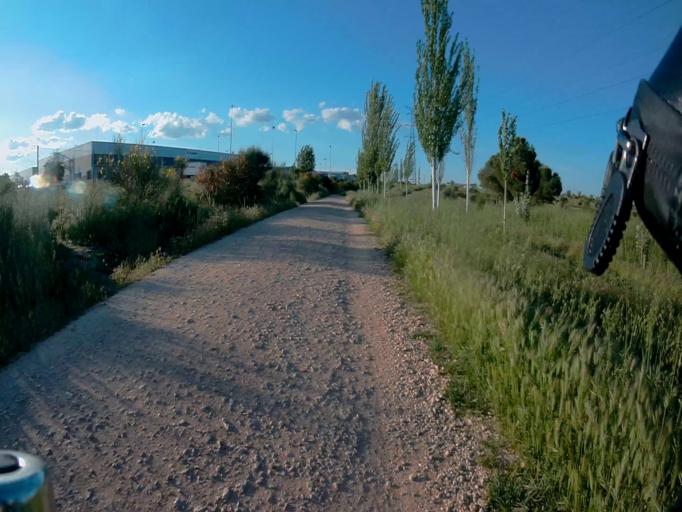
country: ES
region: Madrid
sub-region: Provincia de Madrid
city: Fuenlabrada
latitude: 40.3034
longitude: -3.7989
